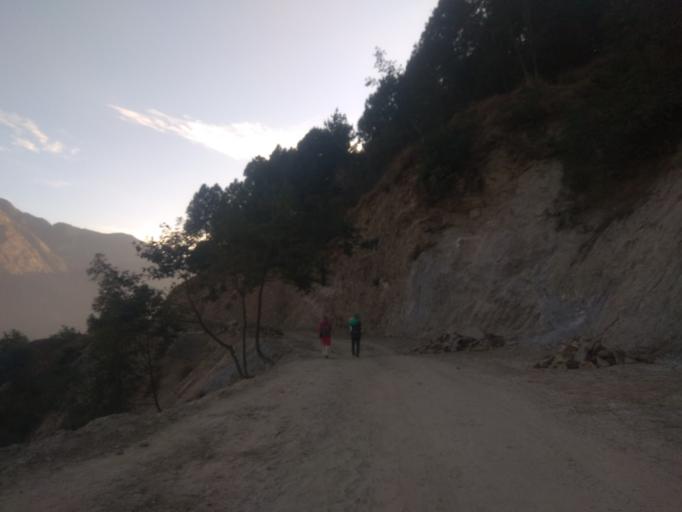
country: NP
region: Far Western
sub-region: Seti Zone
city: Achham
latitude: 29.2462
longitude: 81.6459
